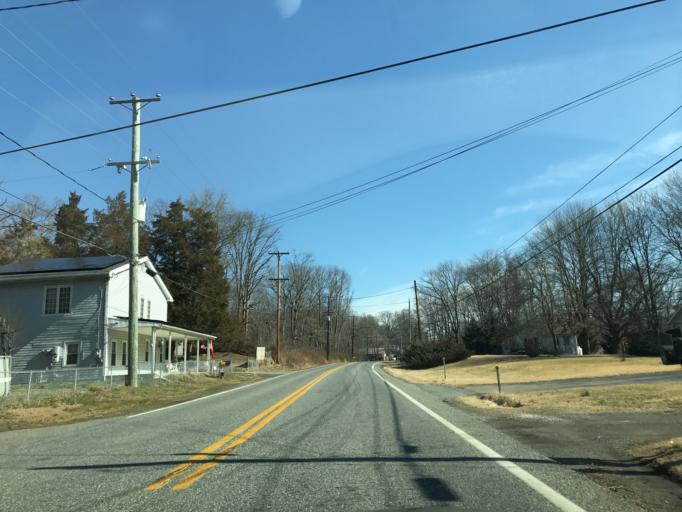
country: US
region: Maryland
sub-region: Cecil County
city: North East
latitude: 39.5967
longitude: -75.9658
